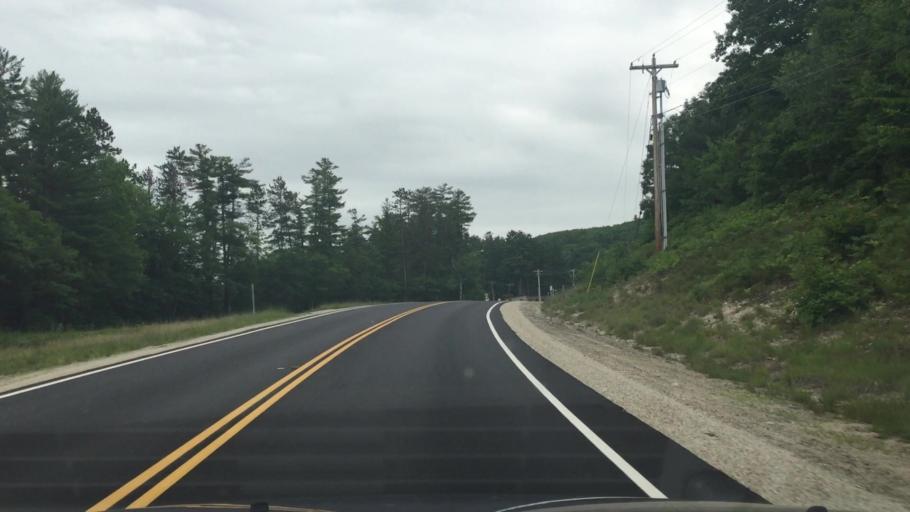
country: US
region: New Hampshire
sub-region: Carroll County
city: Madison
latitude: 43.8712
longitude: -71.0870
